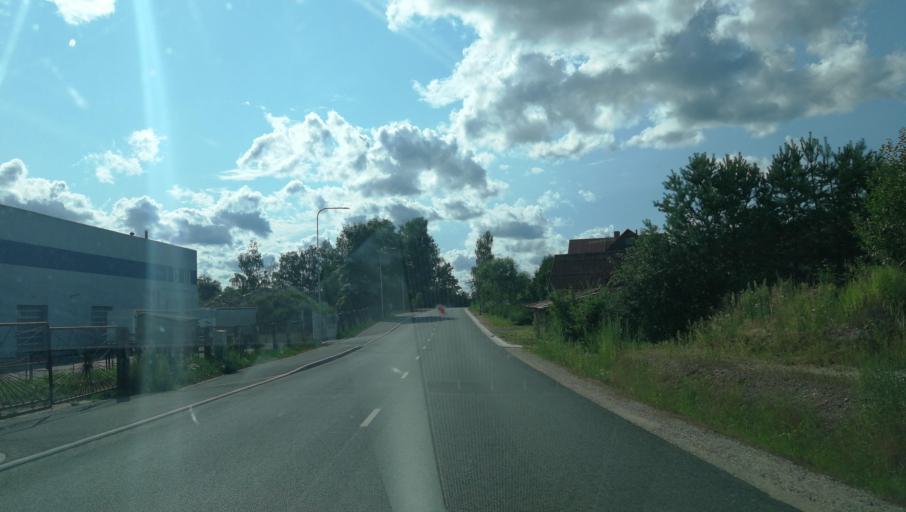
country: LV
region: Cesu Rajons
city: Cesis
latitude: 57.3234
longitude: 25.3015
